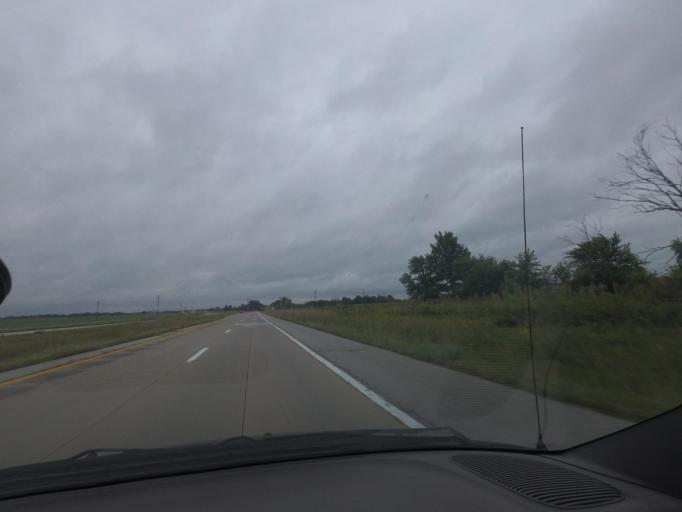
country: US
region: Missouri
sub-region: Marion County
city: Monroe City
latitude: 39.6590
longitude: -91.8124
